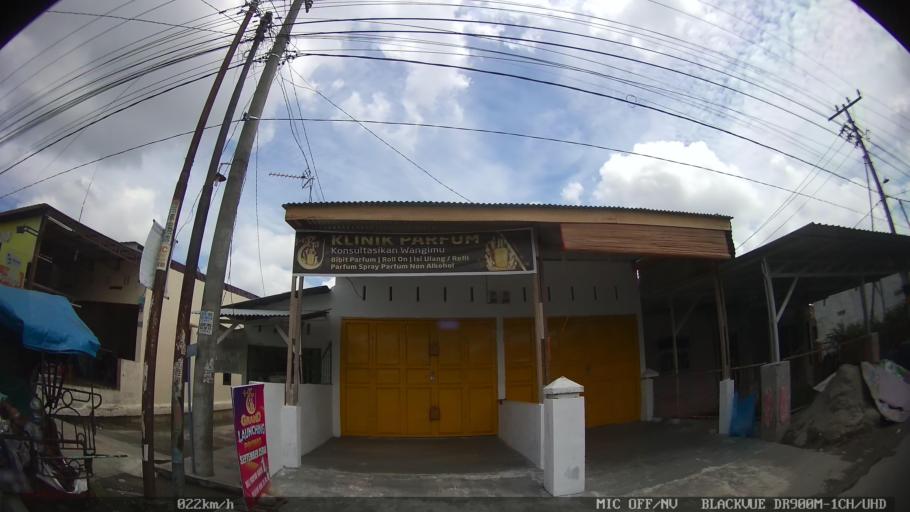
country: ID
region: North Sumatra
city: Medan
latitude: 3.6071
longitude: 98.7544
